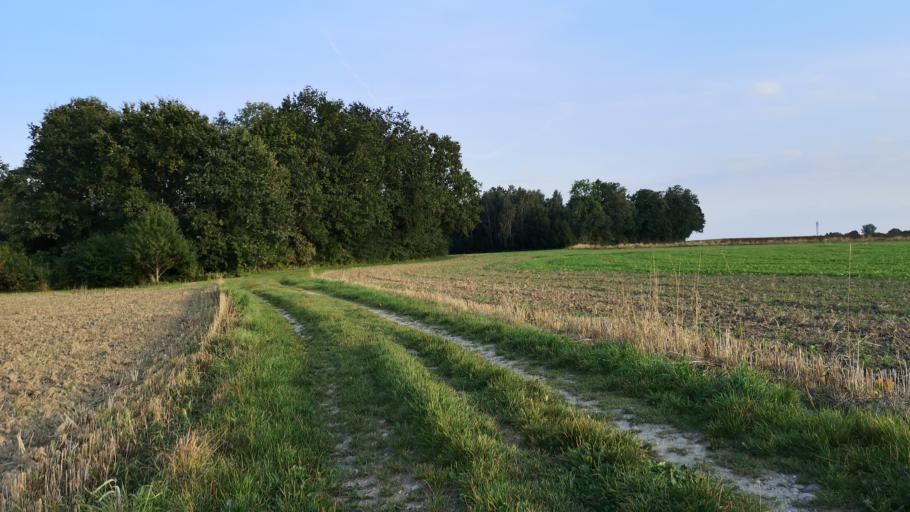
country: DE
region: Bavaria
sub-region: Upper Bavaria
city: Poing
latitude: 48.1635
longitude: 11.8215
